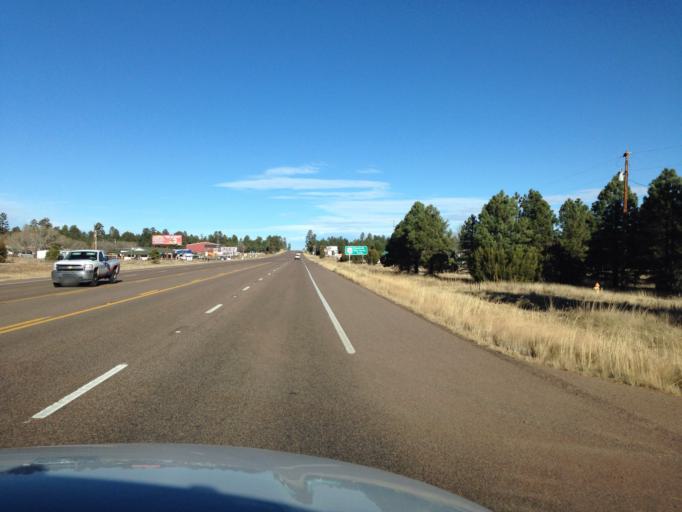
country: US
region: Arizona
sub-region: Navajo County
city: Heber-Overgaard
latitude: 34.4018
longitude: -110.5630
